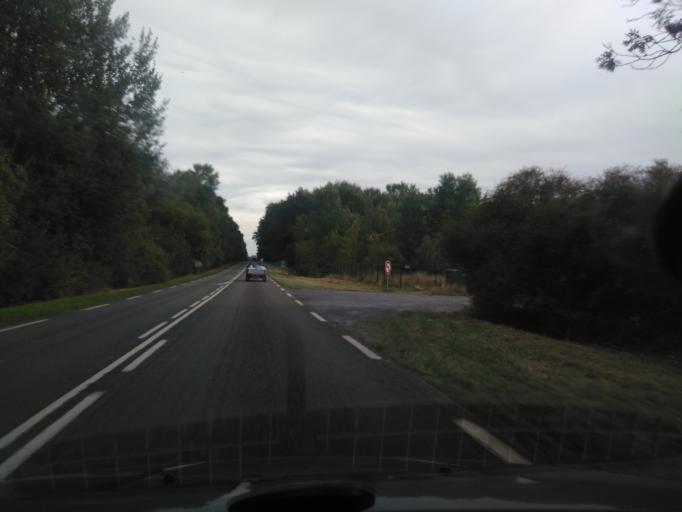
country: FR
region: Picardie
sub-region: Departement de l'Aisne
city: Laon
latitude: 49.5599
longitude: 3.5929
